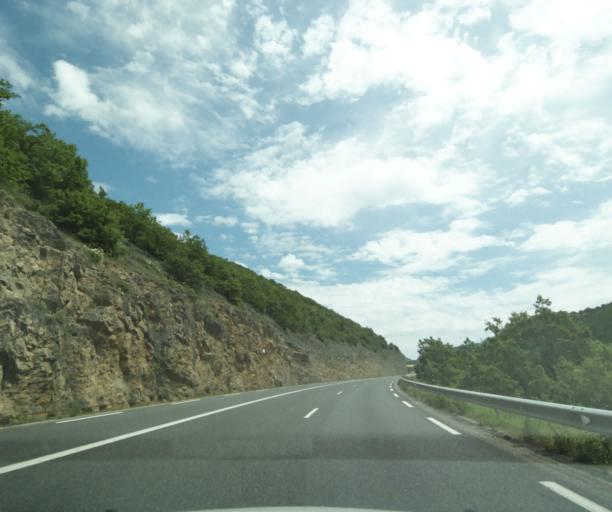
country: FR
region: Midi-Pyrenees
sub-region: Departement de l'Aveyron
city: Saint-Affrique
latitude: 43.9570
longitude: 2.9549
